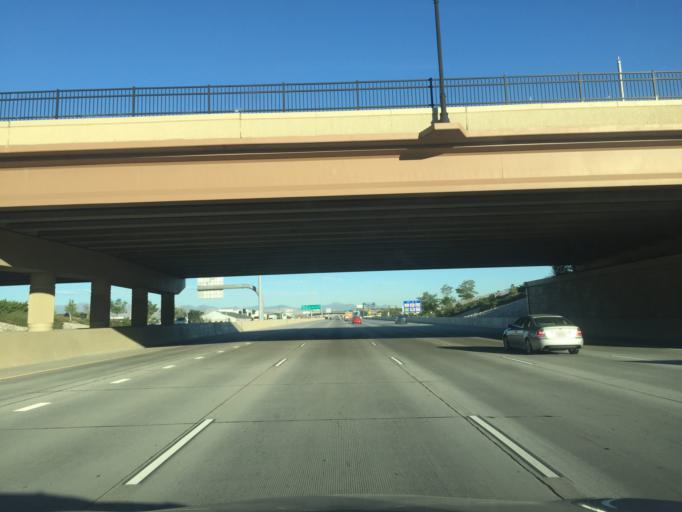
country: US
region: Utah
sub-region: Utah County
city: Pleasant Grove
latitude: 40.3497
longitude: -111.7683
